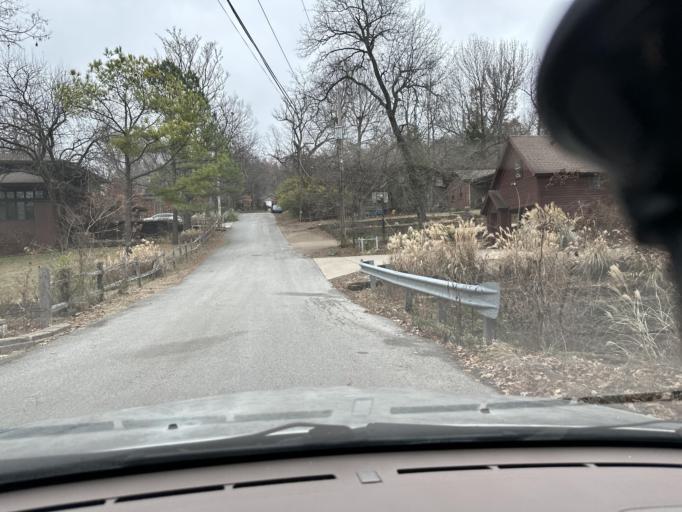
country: US
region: Arkansas
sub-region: Washington County
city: Fayetteville
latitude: 36.0674
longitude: -94.1530
